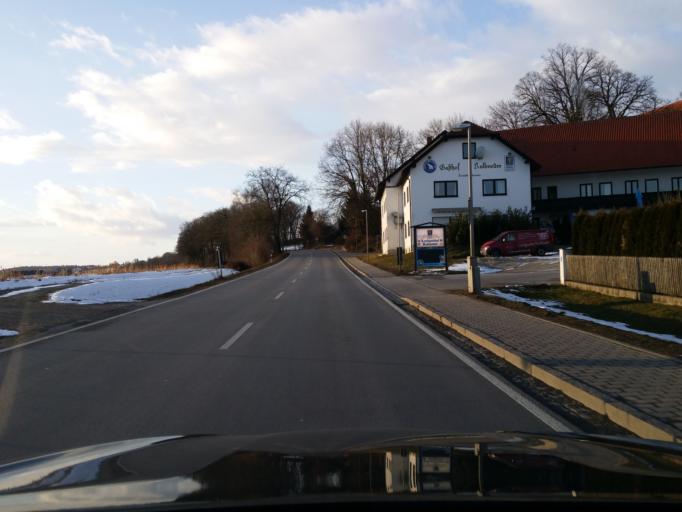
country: DE
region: Bavaria
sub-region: Lower Bavaria
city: Weihmichl
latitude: 48.5848
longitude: 12.0601
